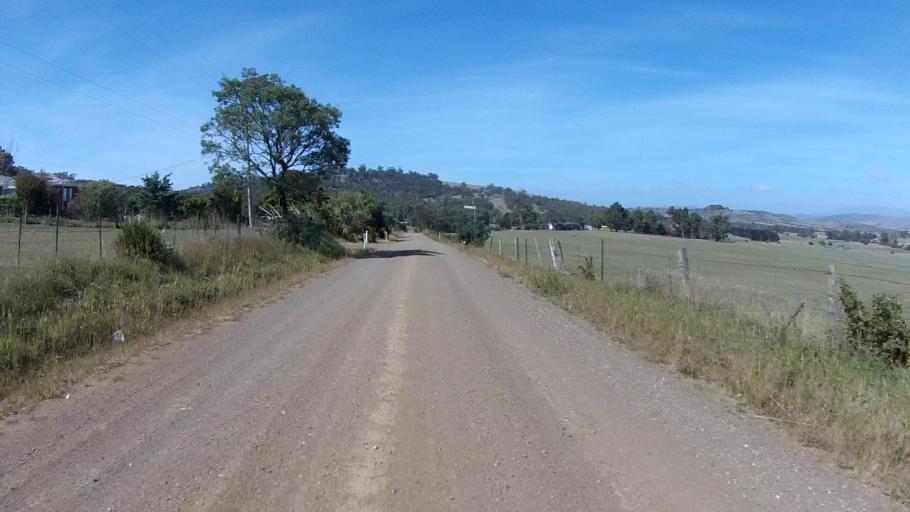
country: AU
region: Tasmania
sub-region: Sorell
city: Sorell
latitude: -42.7284
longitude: 147.5964
